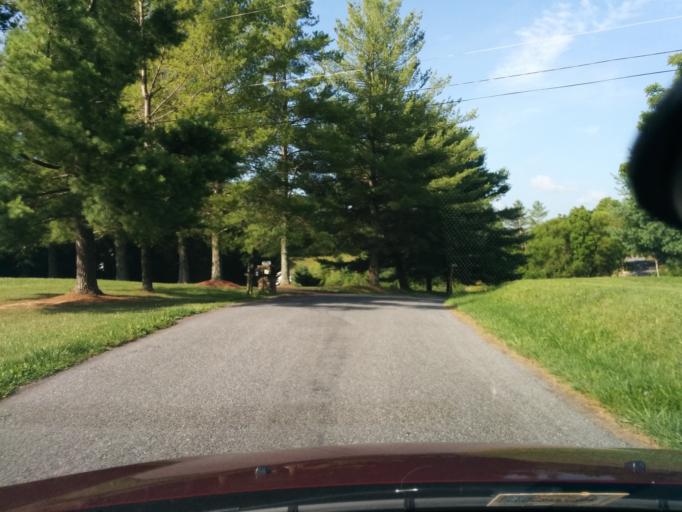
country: US
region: Virginia
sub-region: City of Lexington
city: Lexington
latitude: 37.7746
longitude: -79.4693
